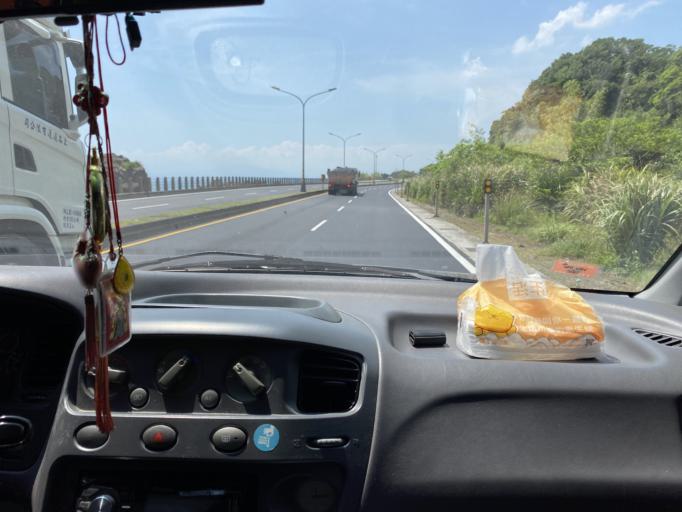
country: TW
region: Taiwan
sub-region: Yilan
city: Yilan
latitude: 24.8959
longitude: 121.8596
